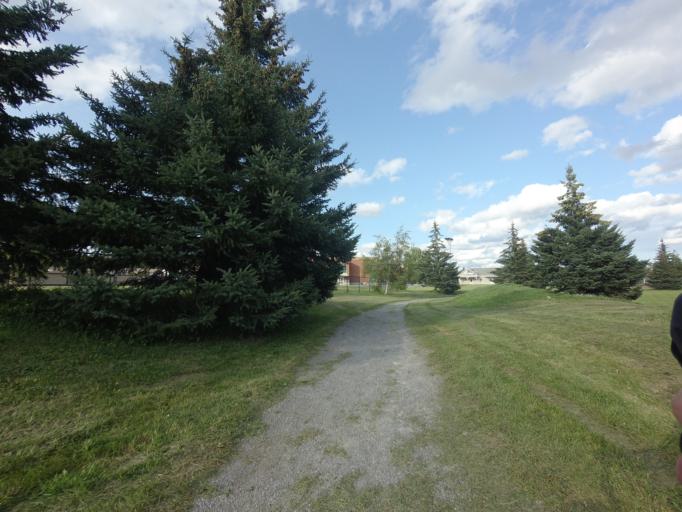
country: CA
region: Ontario
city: Bells Corners
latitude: 45.2876
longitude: -75.7175
